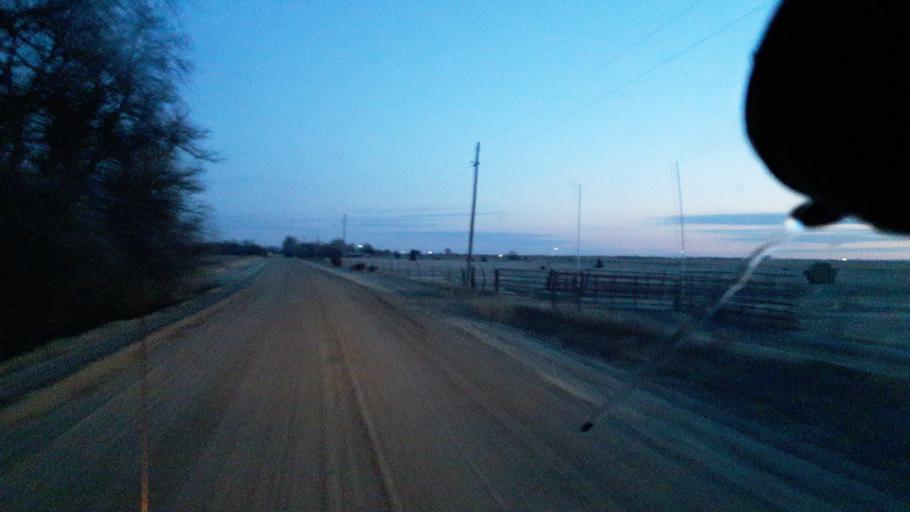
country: US
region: Kansas
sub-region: Reno County
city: South Hutchinson
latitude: 37.9911
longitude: -97.9769
